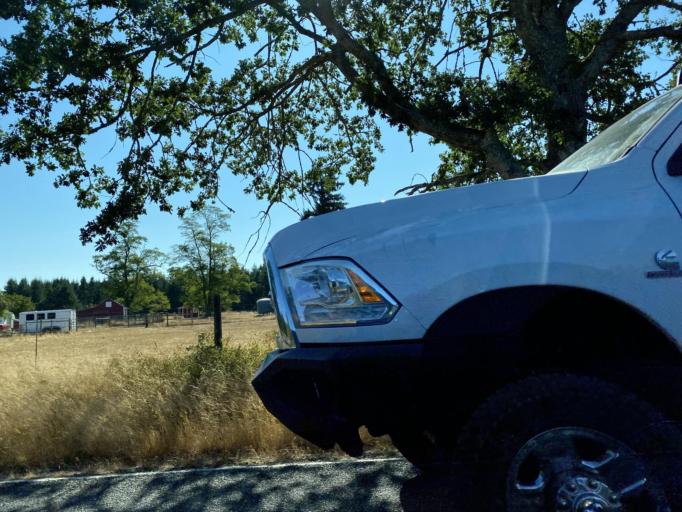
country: US
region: Washington
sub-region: Thurston County
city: Rainier
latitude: 46.8942
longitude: -122.7324
